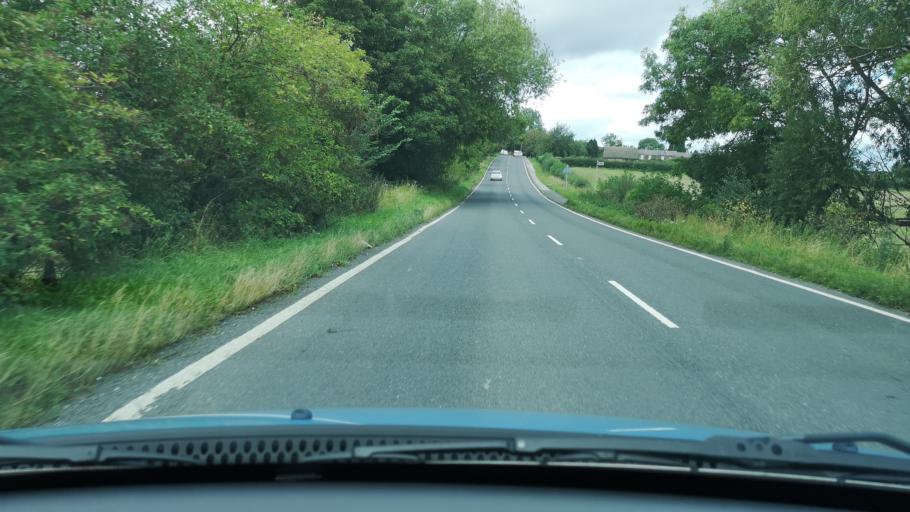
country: GB
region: England
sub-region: City and Borough of Wakefield
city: Low Ackworth
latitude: 53.6372
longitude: -1.3281
